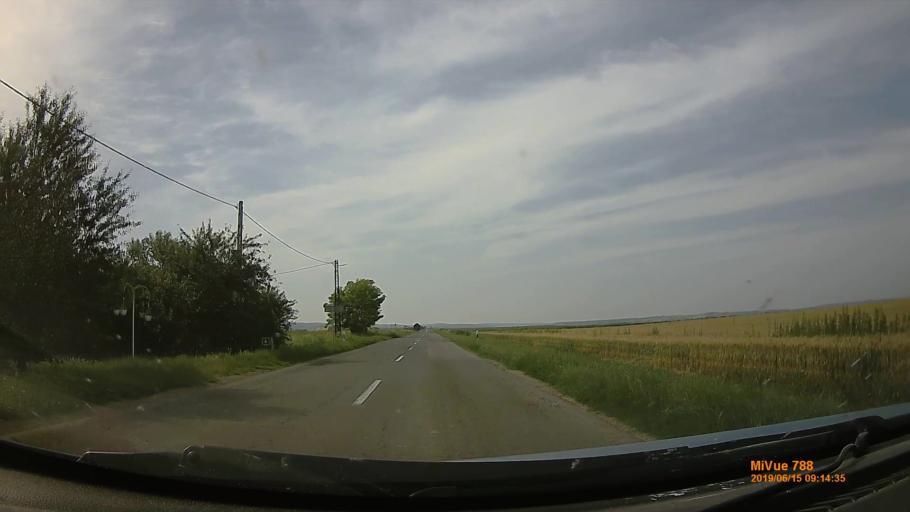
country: HU
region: Tolna
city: Iregszemcse
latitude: 46.6412
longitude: 18.1970
